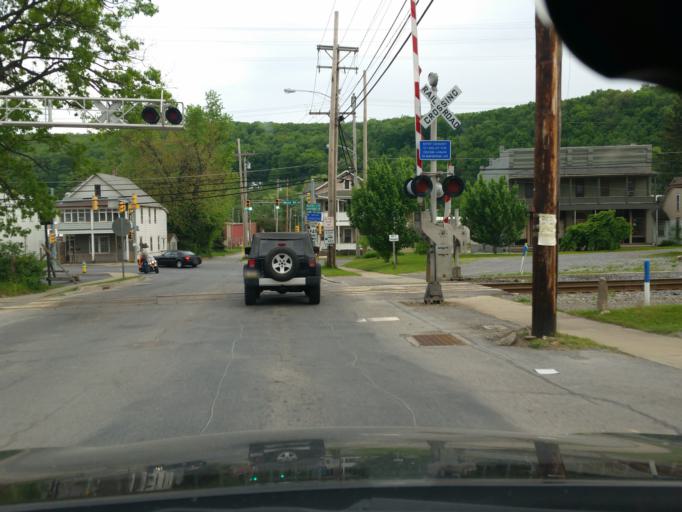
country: US
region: Pennsylvania
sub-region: Elk County
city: Ridgway
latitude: 41.4214
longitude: -78.7390
